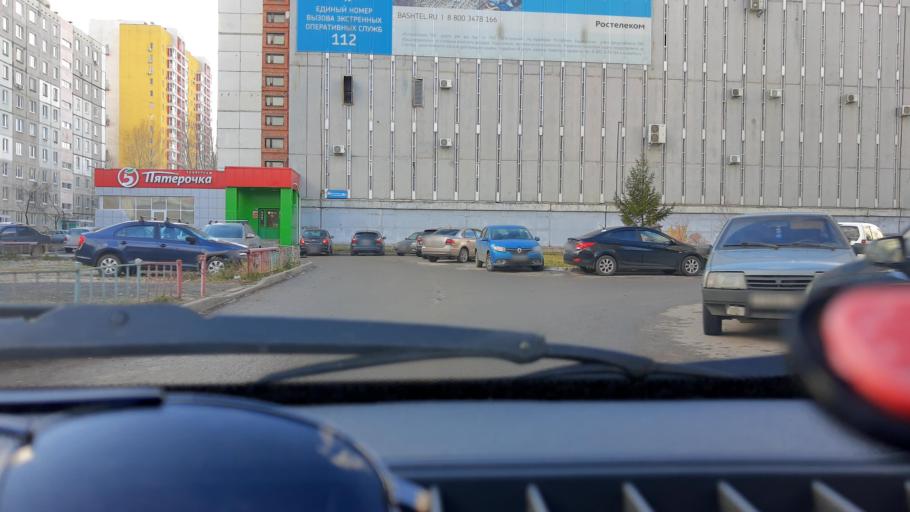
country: RU
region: Bashkortostan
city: Ufa
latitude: 54.7712
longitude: 56.0751
